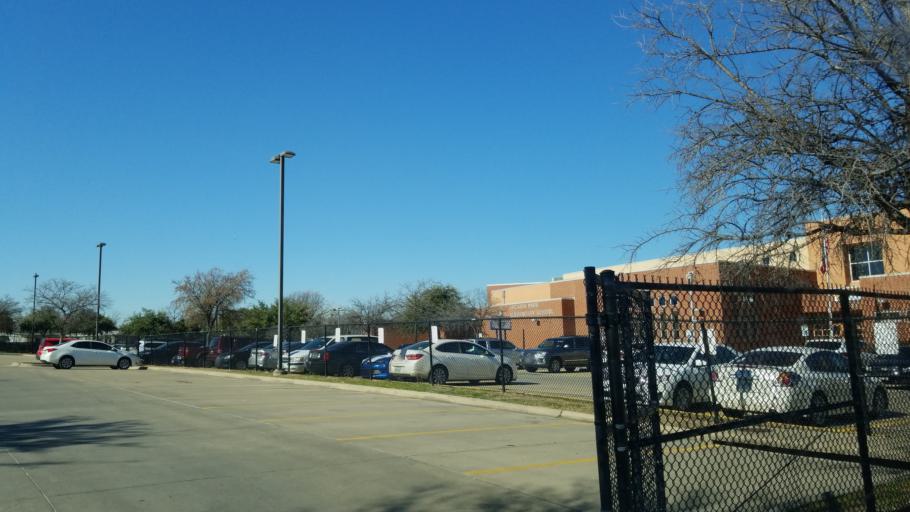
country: US
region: Texas
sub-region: Dallas County
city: Cockrell Hill
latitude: 32.7584
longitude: -96.9102
